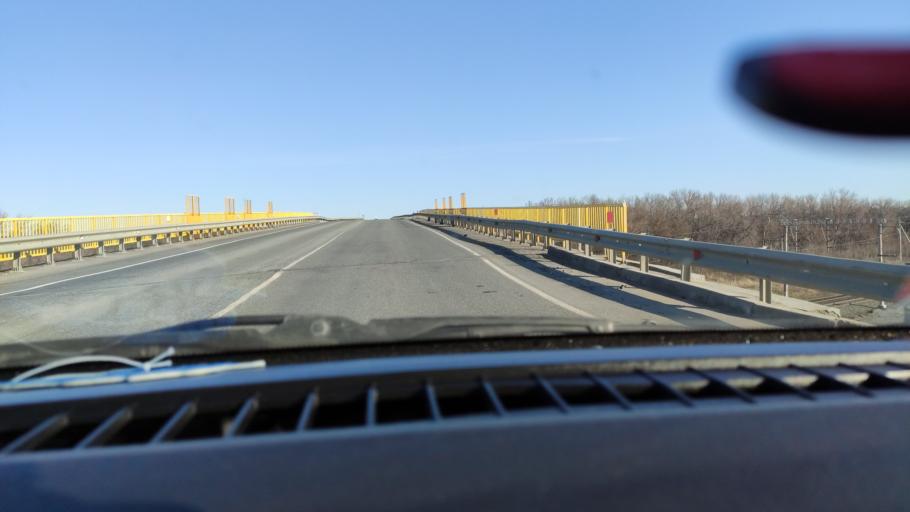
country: RU
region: Saratov
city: Dukhovnitskoye
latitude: 52.7517
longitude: 48.2478
